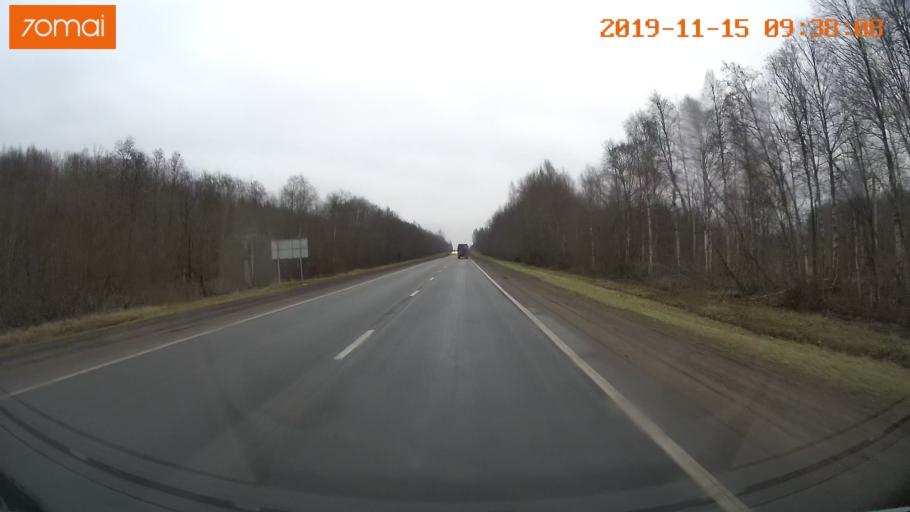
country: RU
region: Vologda
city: Sheksna
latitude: 59.2346
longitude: 38.4498
